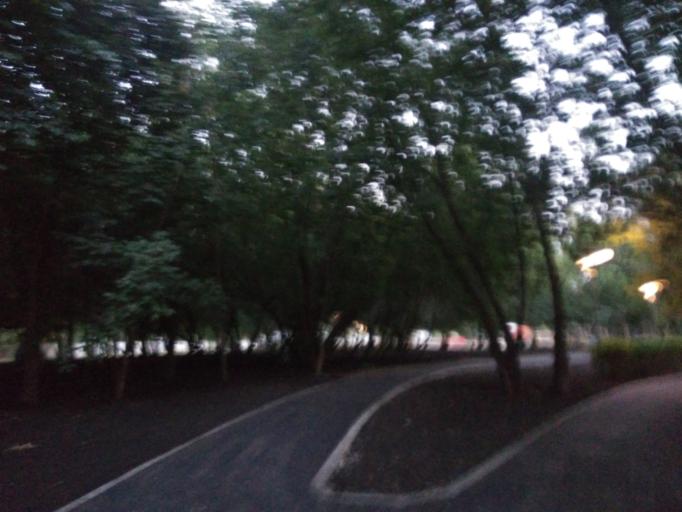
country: RU
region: Moskovskaya
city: Levoberezhnaya
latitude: 55.8776
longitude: 37.4674
